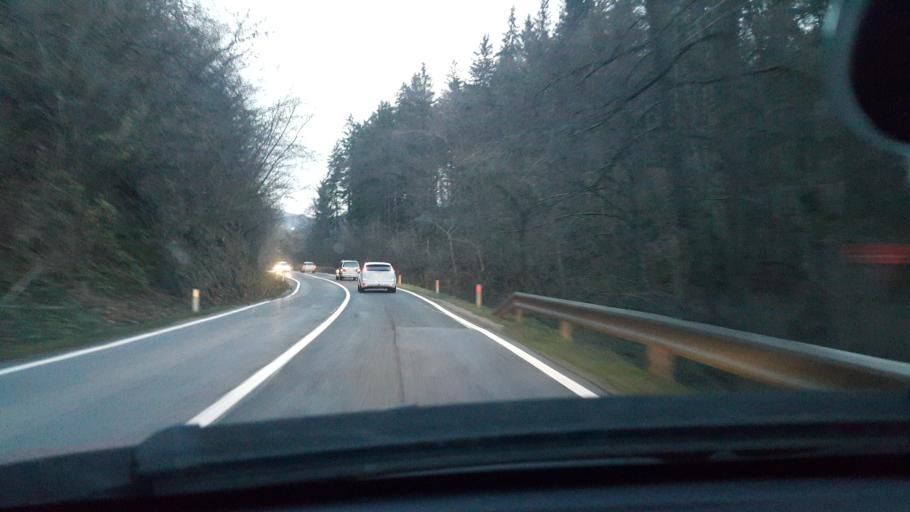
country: SI
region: Dobrna
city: Dobrna
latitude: 46.3287
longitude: 15.1777
